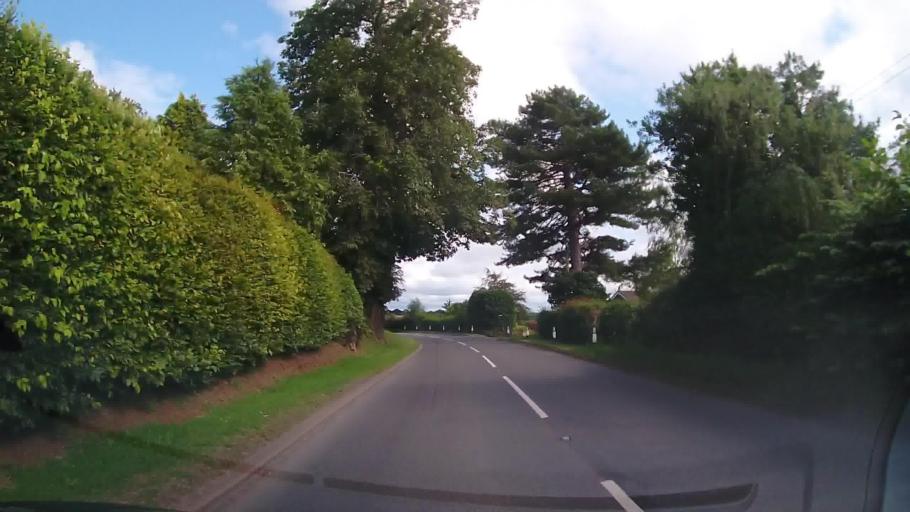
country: GB
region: England
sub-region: Shropshire
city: Pant
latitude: 52.8003
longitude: -3.0101
